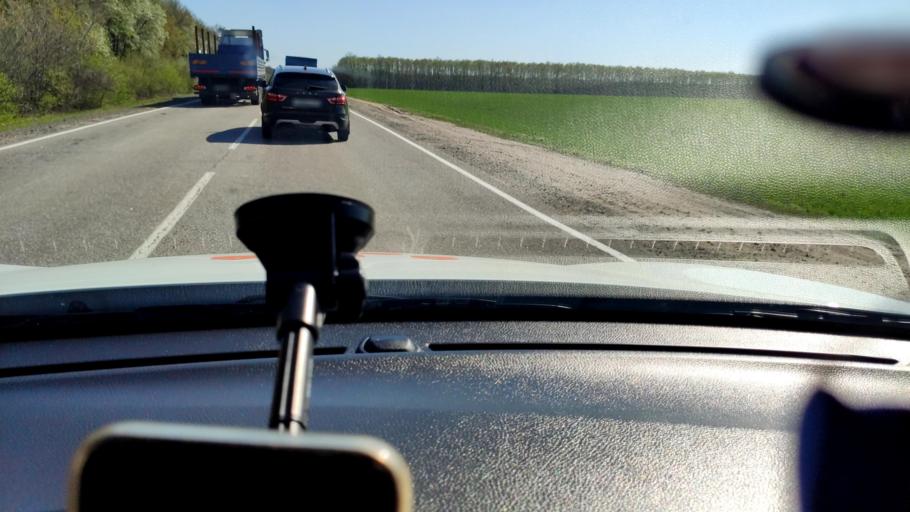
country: RU
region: Voronezj
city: Shilovo
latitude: 51.4249
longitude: 39.0082
